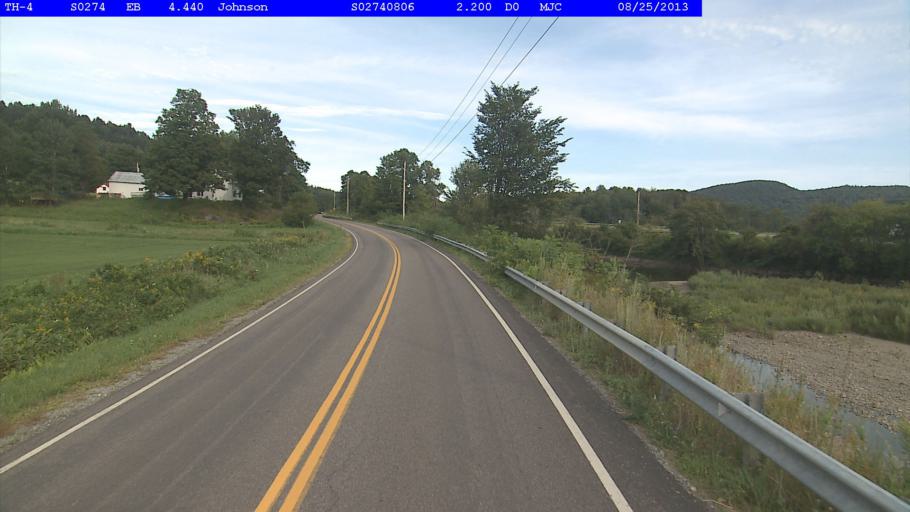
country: US
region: Vermont
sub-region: Lamoille County
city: Johnson
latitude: 44.6435
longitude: -72.7134
